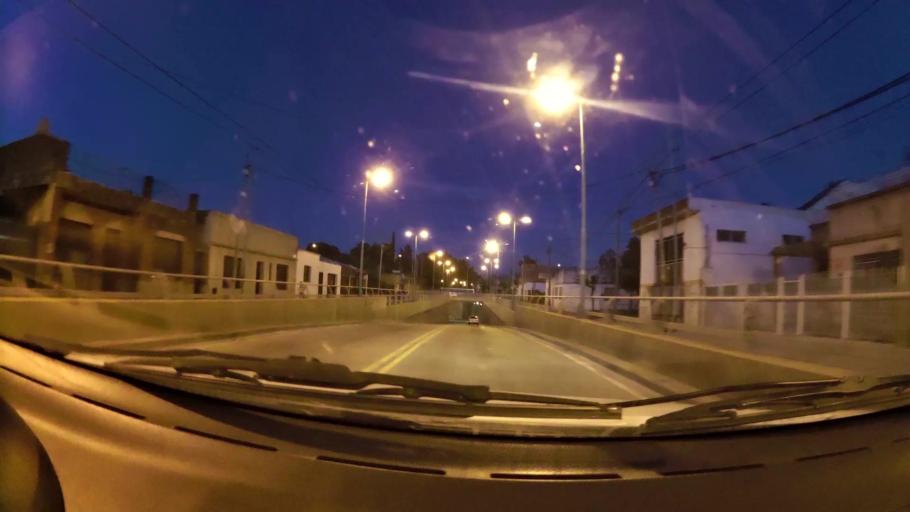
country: AR
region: Buenos Aires
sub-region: Partido de Quilmes
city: Quilmes
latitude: -34.7750
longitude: -58.1883
